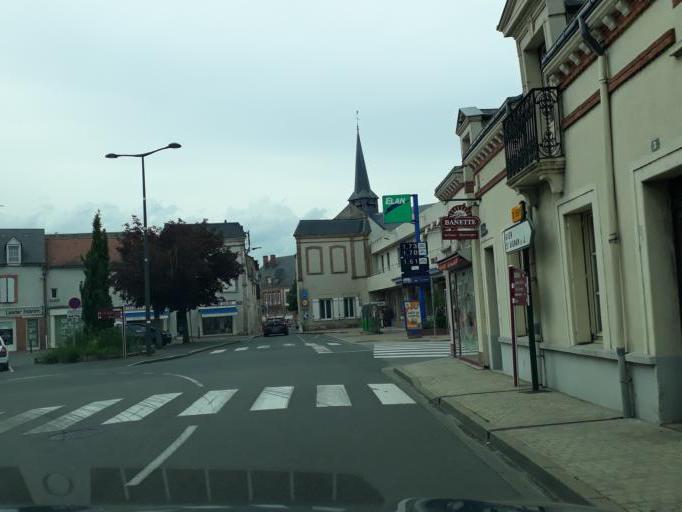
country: FR
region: Centre
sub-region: Departement du Loiret
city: Sully-sur-Loire
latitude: 47.7648
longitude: 2.3773
